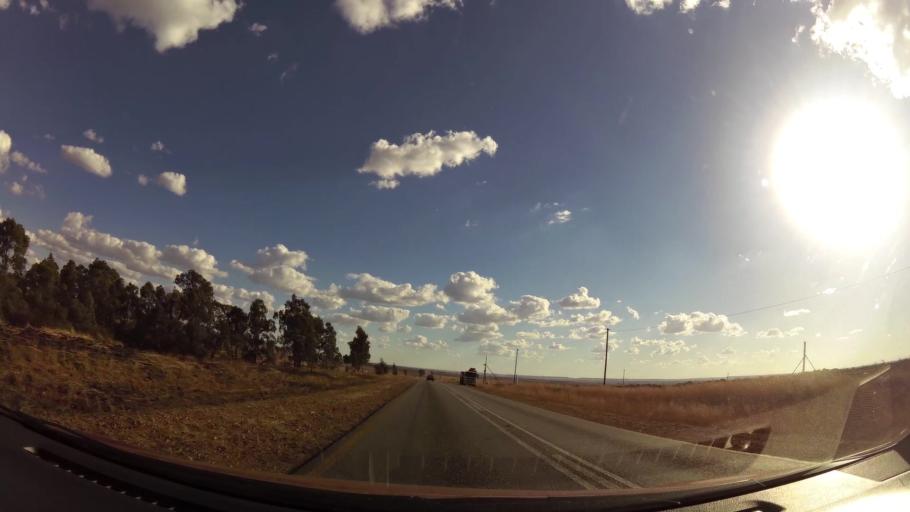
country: ZA
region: Gauteng
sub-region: West Rand District Municipality
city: Carletonville
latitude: -26.3996
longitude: 27.2945
